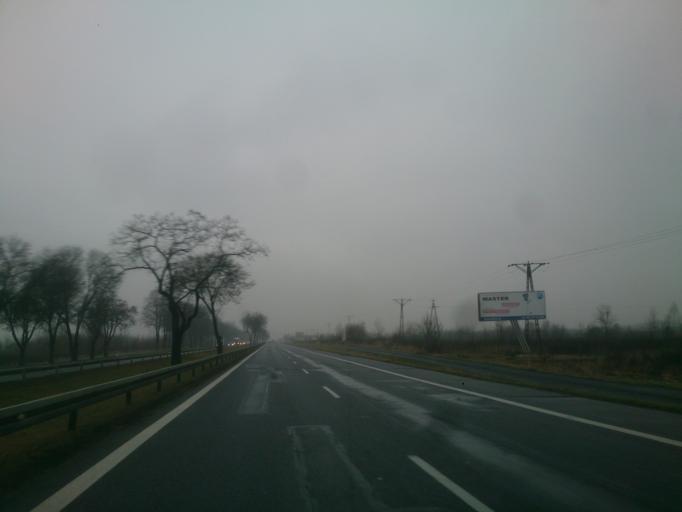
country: PL
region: Masovian Voivodeship
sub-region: Powiat warszawski zachodni
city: Truskaw
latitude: 52.3769
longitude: 20.7754
